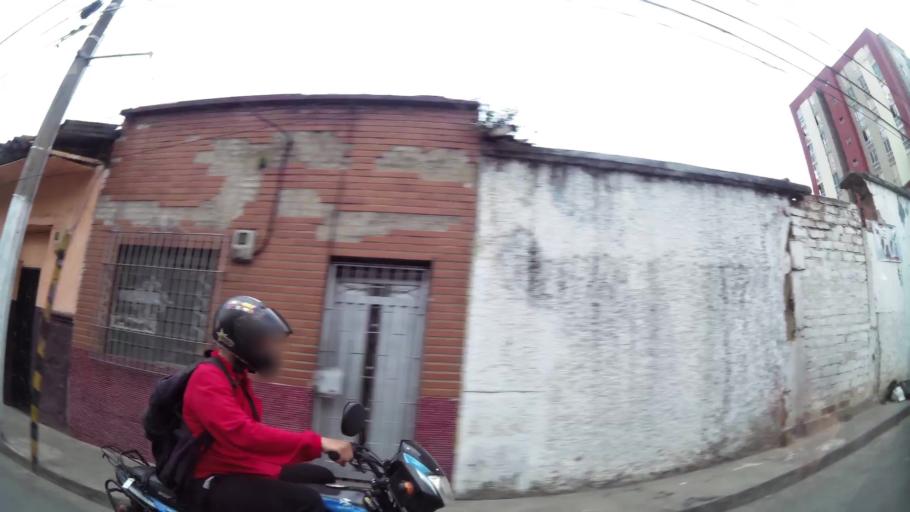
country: CO
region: Antioquia
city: Medellin
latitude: 6.2439
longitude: -75.5550
